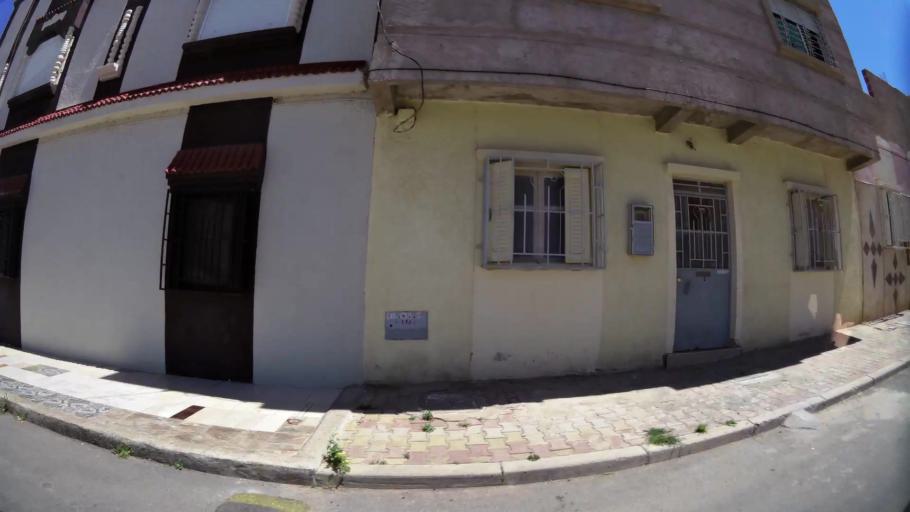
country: MA
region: Oriental
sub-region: Oujda-Angad
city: Oujda
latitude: 34.6558
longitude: -1.9289
